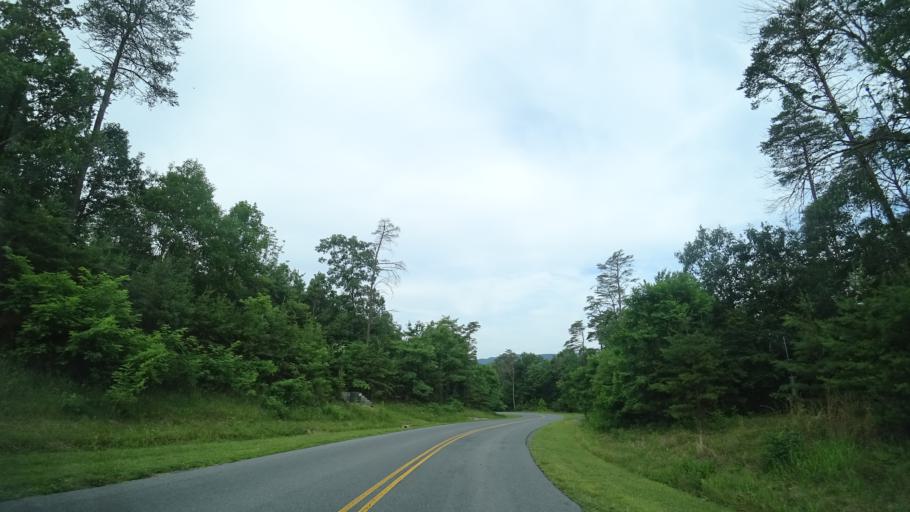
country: US
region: Virginia
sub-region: Warren County
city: Front Royal
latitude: 38.8476
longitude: -78.3076
